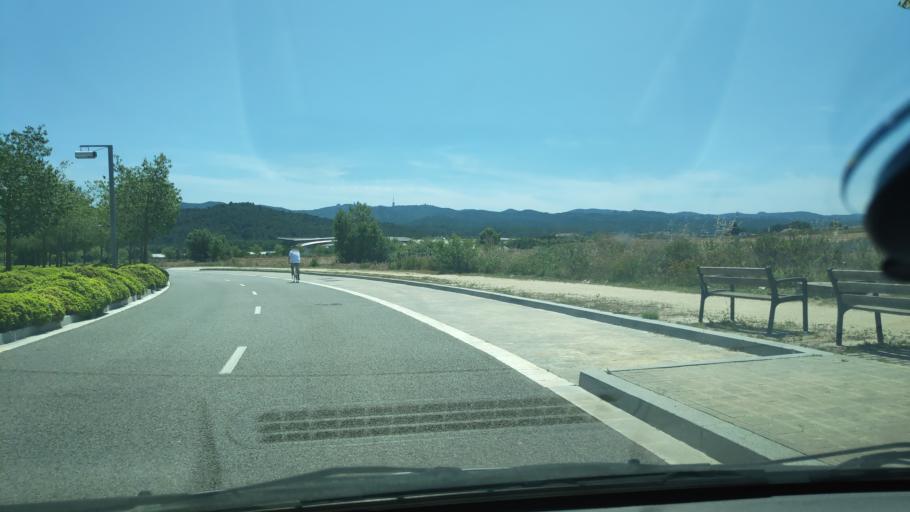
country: ES
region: Catalonia
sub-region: Provincia de Barcelona
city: Barbera del Valles
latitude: 41.4904
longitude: 2.1099
